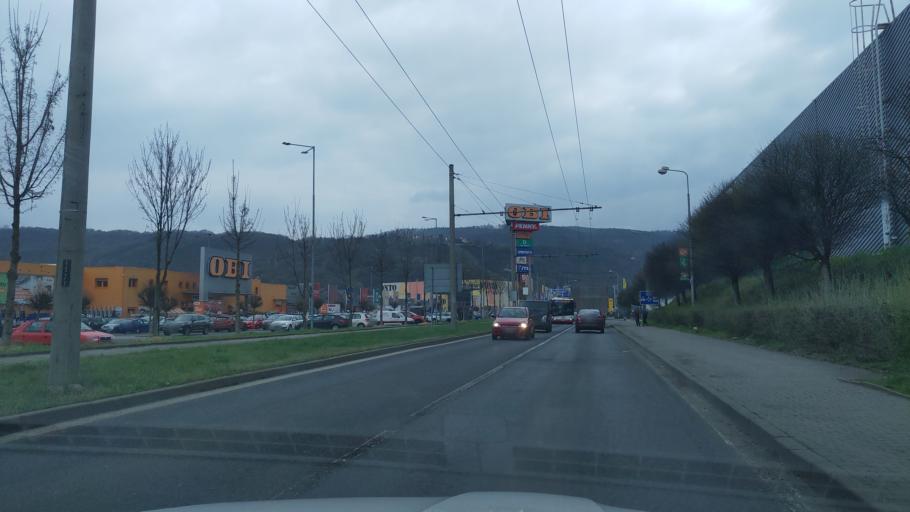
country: CZ
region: Ustecky
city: Trmice
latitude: 50.6520
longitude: 14.0024
